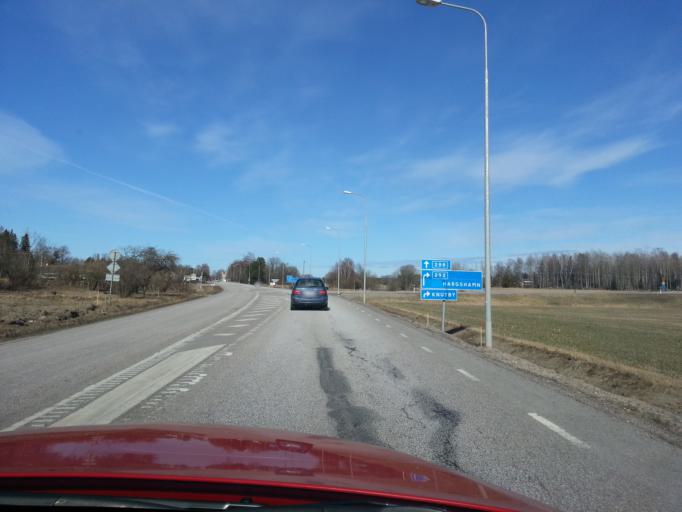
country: SE
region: Uppsala
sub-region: Osthammars Kommun
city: Gimo
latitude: 60.1630
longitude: 18.1934
